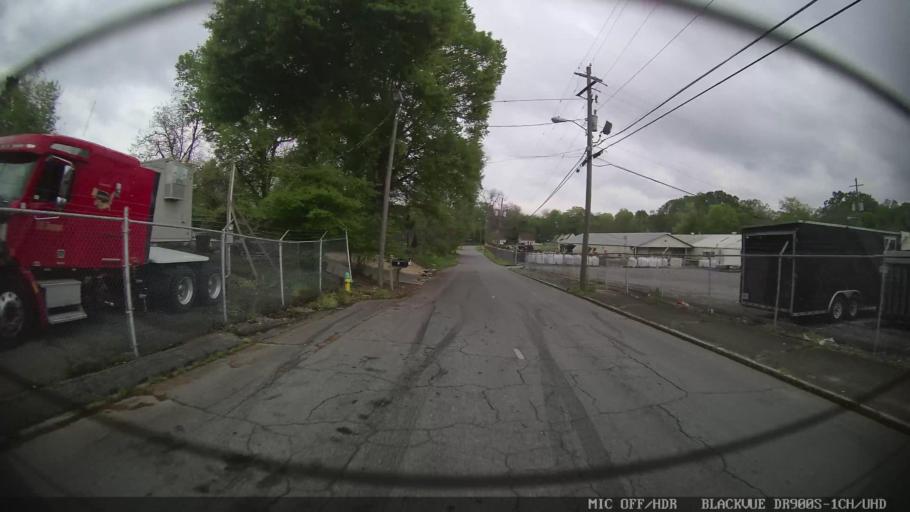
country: US
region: Georgia
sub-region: Bartow County
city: Cartersville
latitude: 34.1737
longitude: -84.7988
